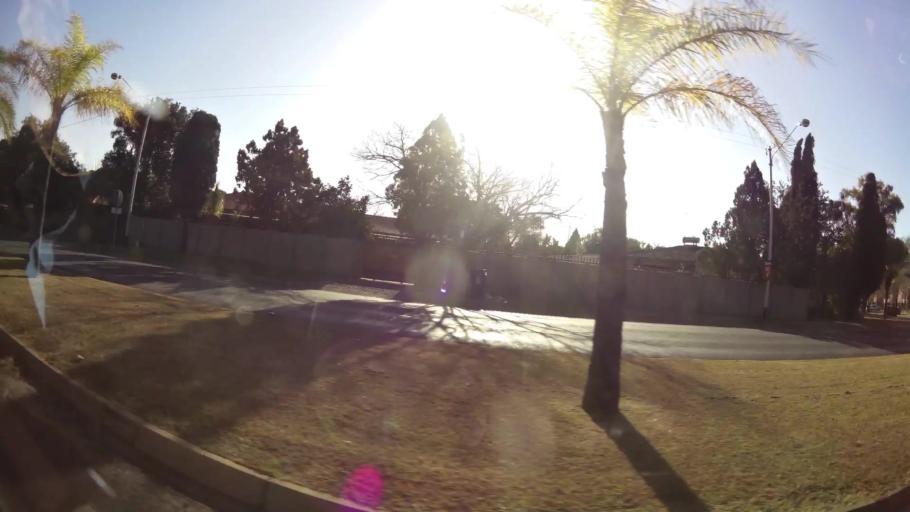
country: ZA
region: Gauteng
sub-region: City of Tshwane Metropolitan Municipality
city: Pretoria
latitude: -25.7111
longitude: 28.2253
